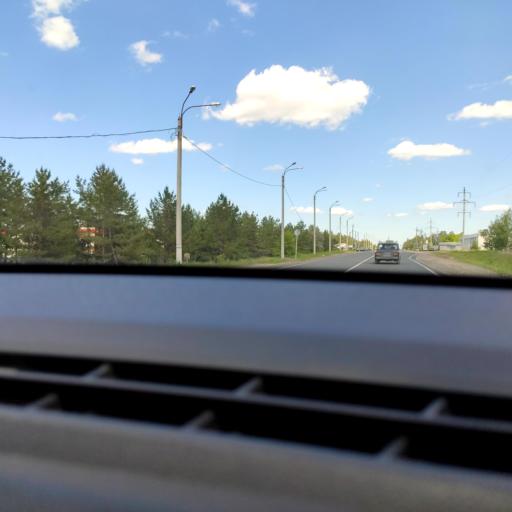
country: RU
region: Samara
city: Zhigulevsk
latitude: 53.5646
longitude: 49.5460
